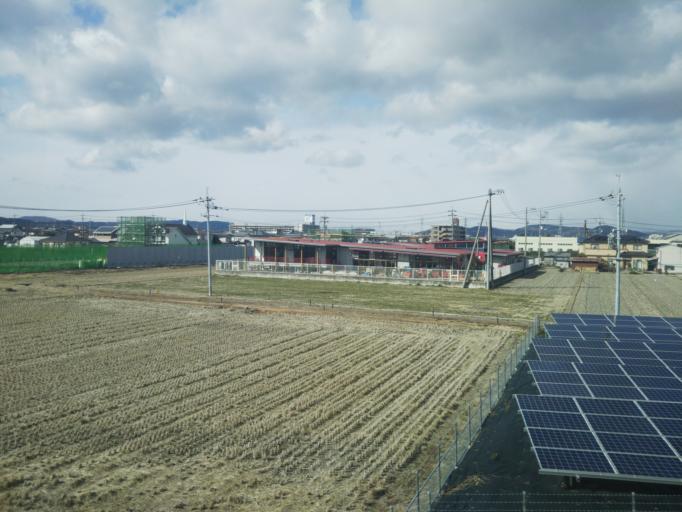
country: JP
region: Okayama
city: Okayama-shi
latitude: 34.6144
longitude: 133.8824
